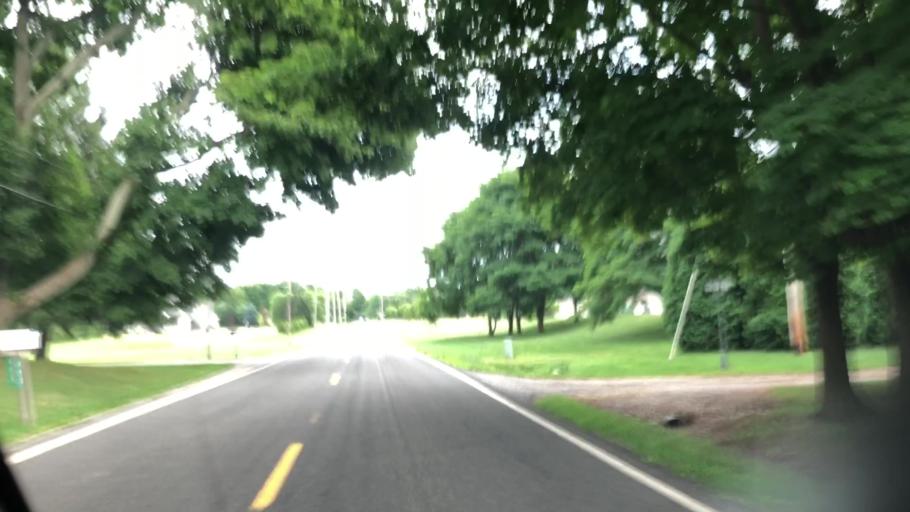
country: US
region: Ohio
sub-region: Summit County
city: Montrose-Ghent
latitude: 41.1178
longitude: -81.7105
